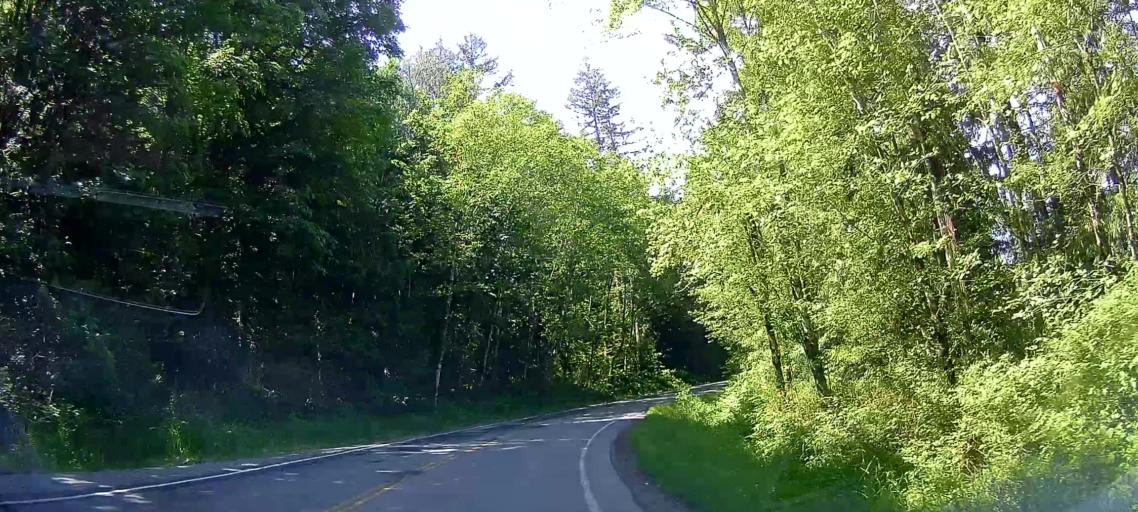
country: US
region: Washington
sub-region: Skagit County
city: Mount Vernon
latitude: 48.3979
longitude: -122.3002
